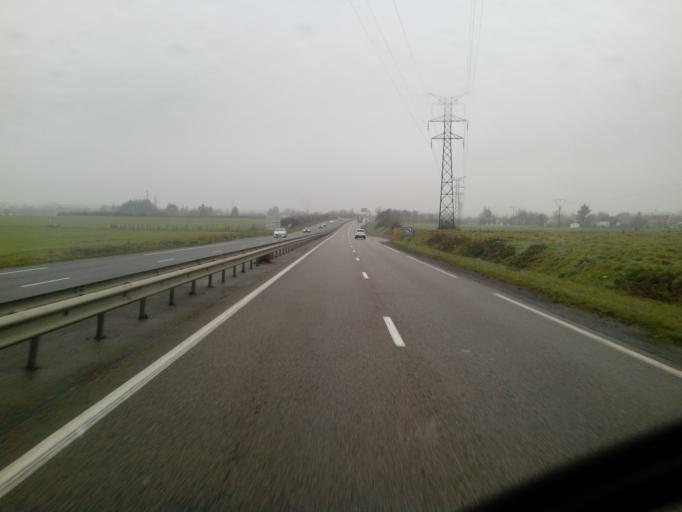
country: FR
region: Poitou-Charentes
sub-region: Departement de la Vienne
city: Mignaloux-Beauvoir
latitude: 46.5792
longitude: 0.3957
